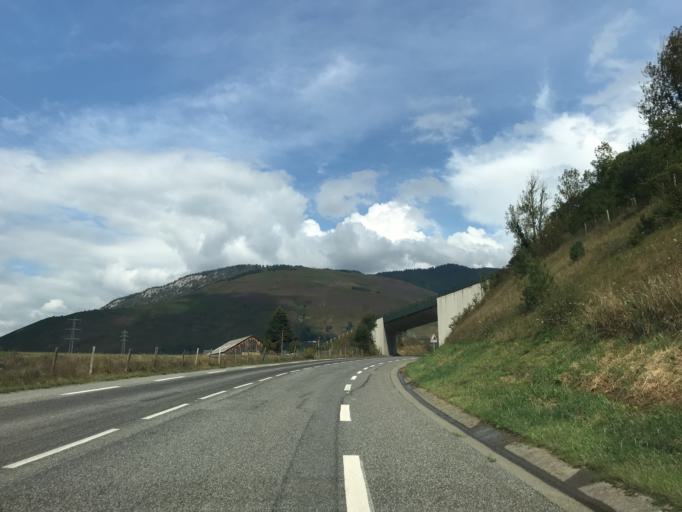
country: FR
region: Midi-Pyrenees
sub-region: Departement des Hautes-Pyrenees
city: Saint-Lary-Soulan
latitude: 42.8970
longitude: 0.3579
